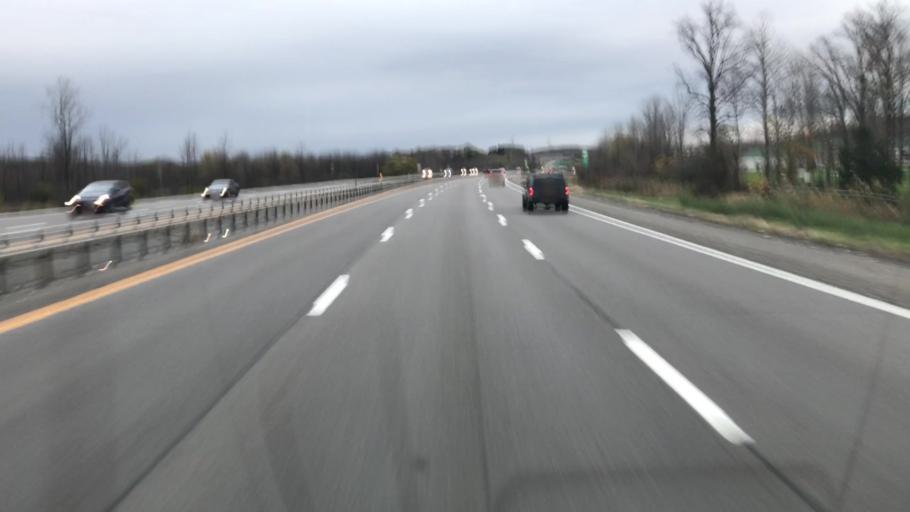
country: US
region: New York
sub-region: Onondaga County
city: Camillus
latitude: 43.0531
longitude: -76.2899
